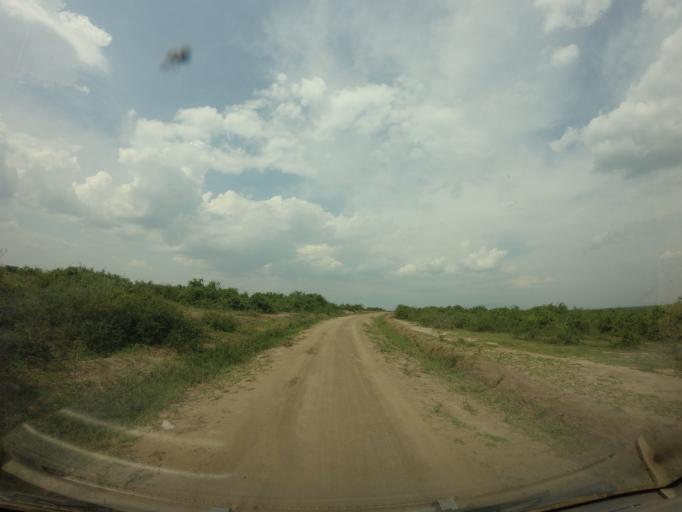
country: UG
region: Western Region
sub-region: Rubirizi District
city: Rubirizi
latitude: -0.2091
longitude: 29.9031
